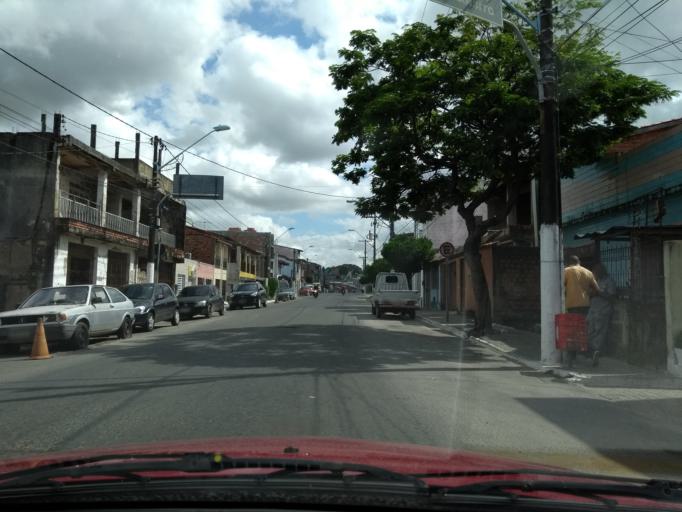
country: BR
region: Bahia
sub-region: Sao Francisco Do Conde
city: Sao Francisco do Conde
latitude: -12.6259
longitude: -38.6758
